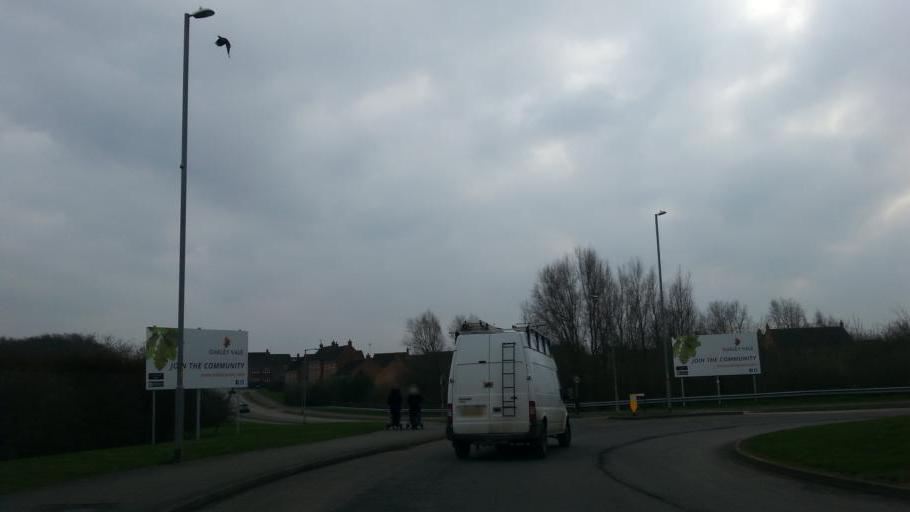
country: GB
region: England
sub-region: Northamptonshire
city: Corby
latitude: 52.4805
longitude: -0.7038
